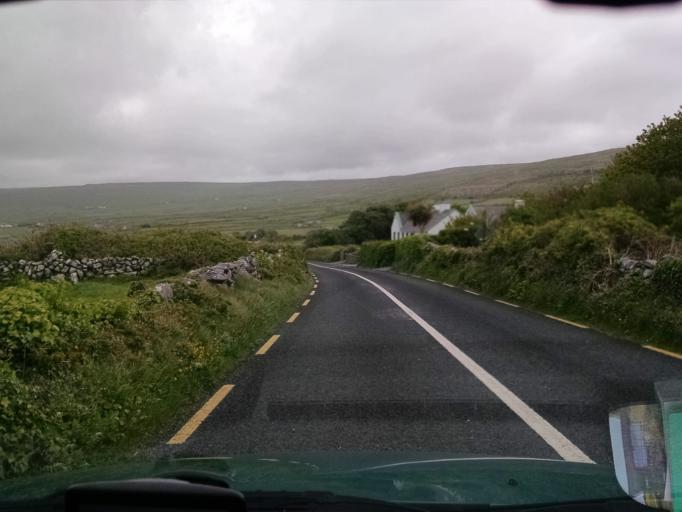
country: IE
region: Connaught
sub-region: County Galway
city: Bearna
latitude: 53.0849
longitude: -9.3237
